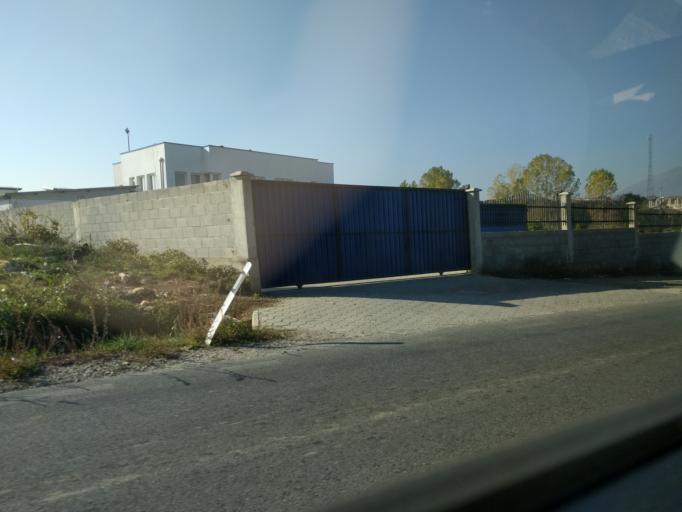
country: XK
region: Prizren
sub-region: Prizren
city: Prizren
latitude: 42.2495
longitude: 20.7257
